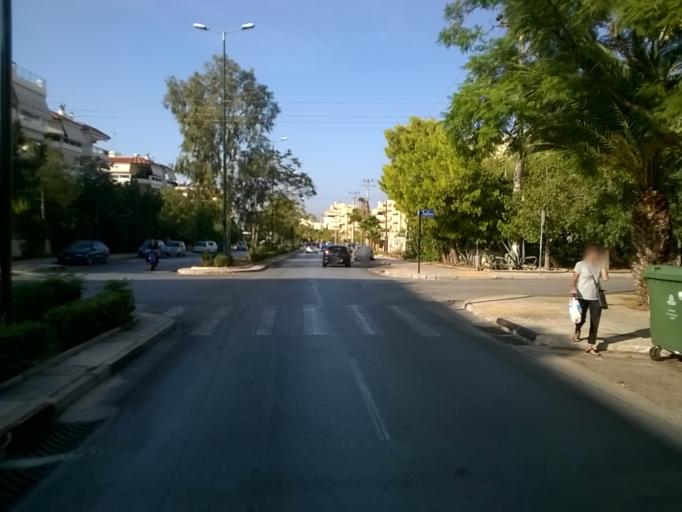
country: GR
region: Attica
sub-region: Nomarchia Athinas
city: Glyfada
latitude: 37.8730
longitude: 23.7629
